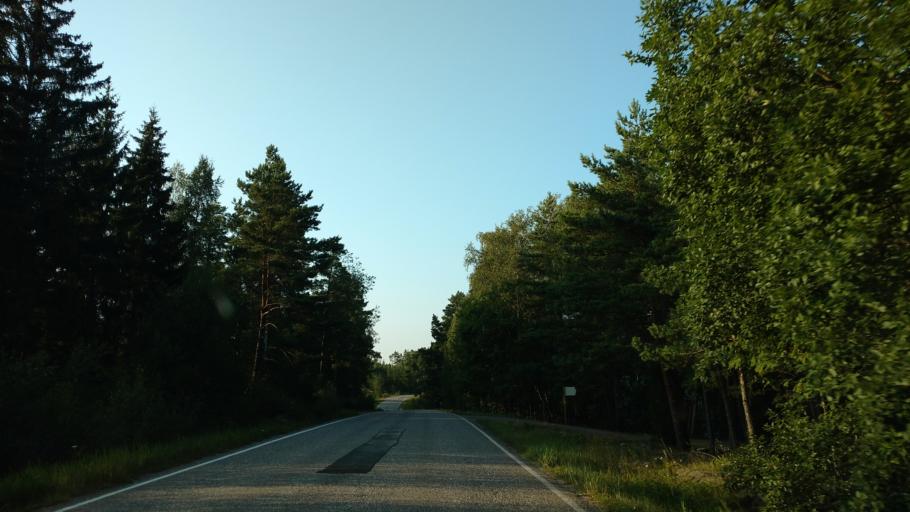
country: FI
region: Varsinais-Suomi
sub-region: Aboland-Turunmaa
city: Dragsfjaerd
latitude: 60.0008
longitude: 22.4536
